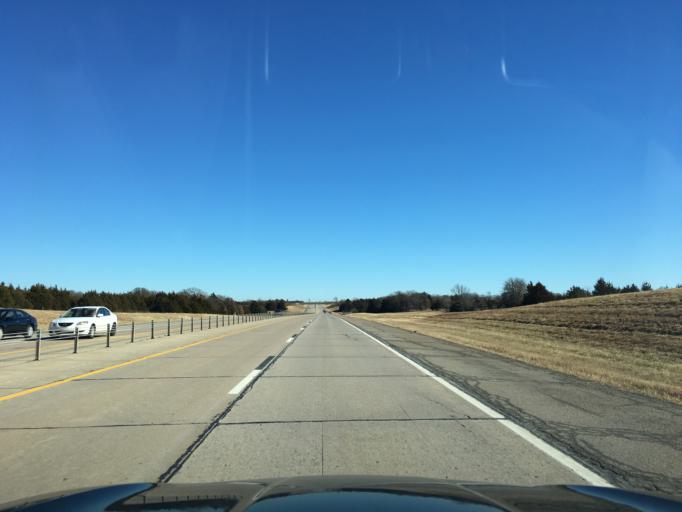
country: US
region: Oklahoma
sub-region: Pawnee County
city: Pawnee
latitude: 36.2248
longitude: -96.8286
